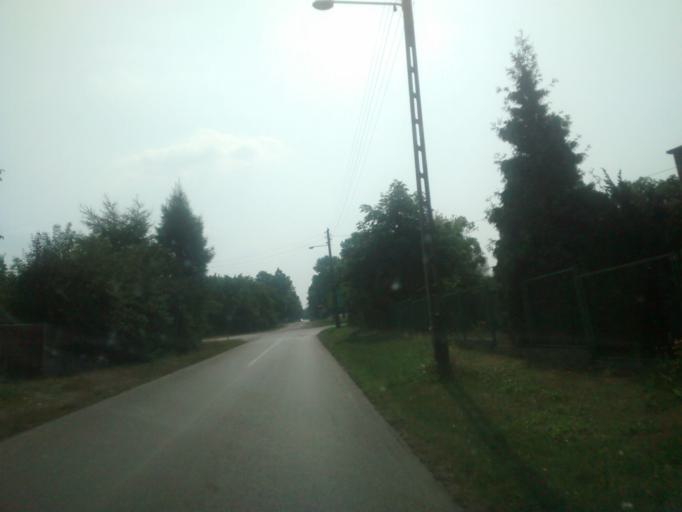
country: PL
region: Silesian Voivodeship
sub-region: Powiat myszkowski
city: Zarki
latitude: 50.6230
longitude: 19.3706
